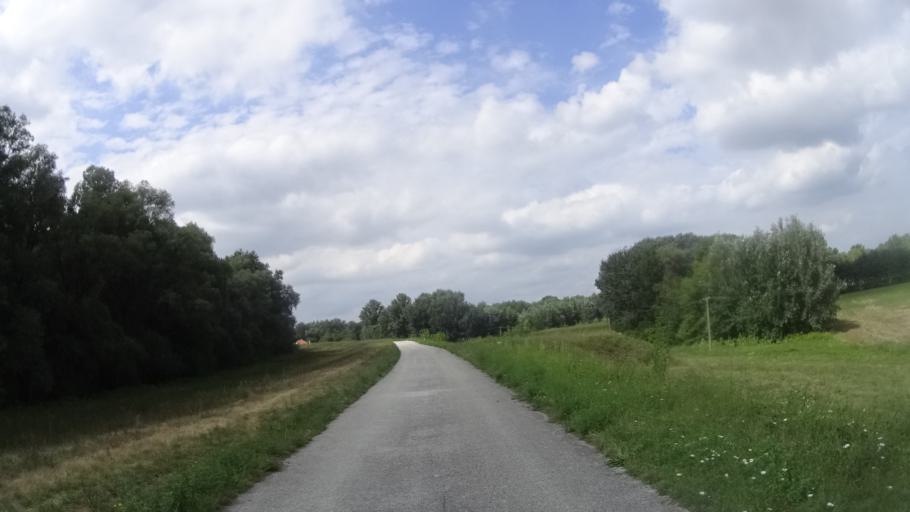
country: SK
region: Trnavsky
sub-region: Okres Dunajska Streda
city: Velky Meder
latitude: 47.7888
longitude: 17.6925
